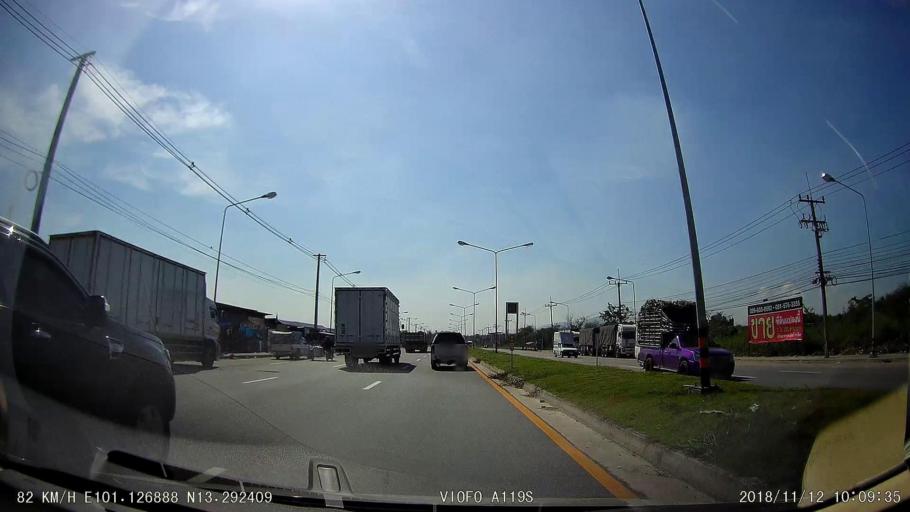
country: TH
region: Chon Buri
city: Ban Bueng
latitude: 13.2922
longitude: 101.1269
